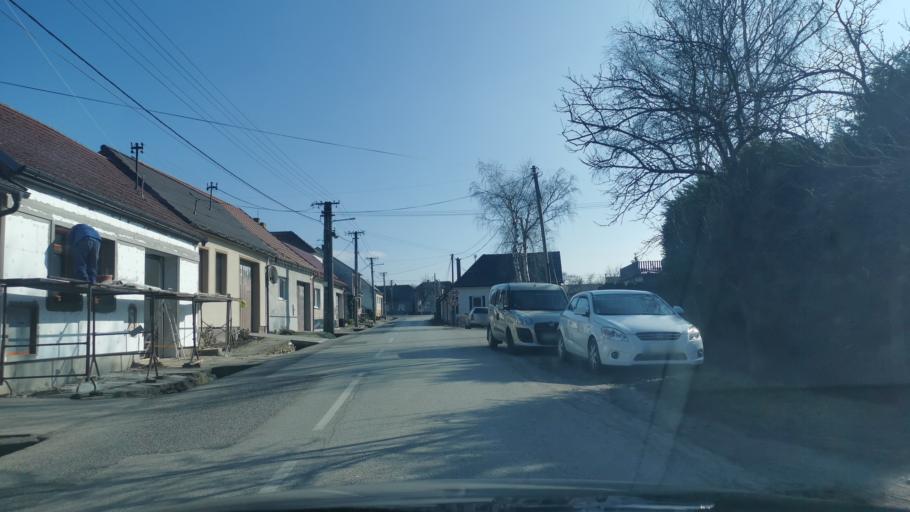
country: SK
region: Trnavsky
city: Gbely
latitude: 48.7177
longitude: 17.1632
